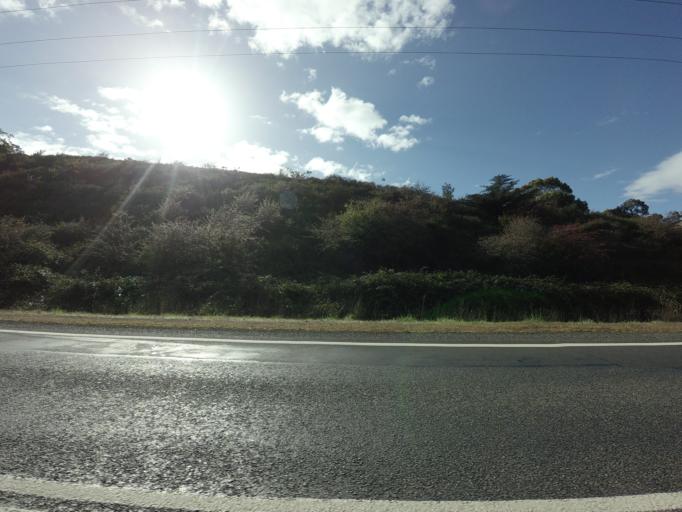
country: AU
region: Tasmania
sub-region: Derwent Valley
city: New Norfolk
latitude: -42.7297
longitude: 146.9568
